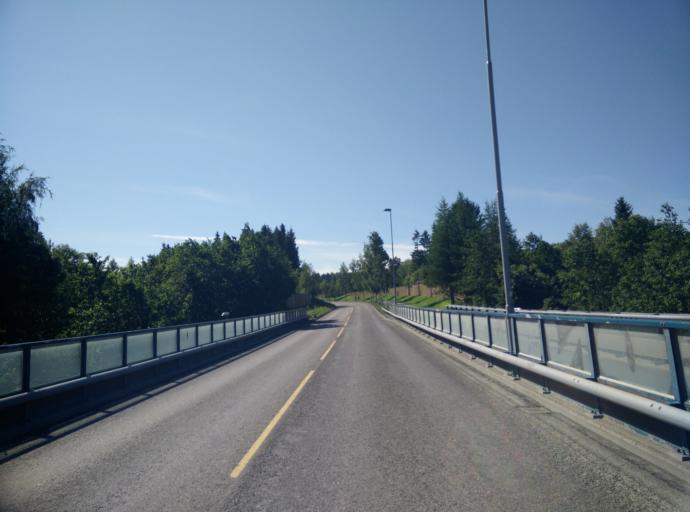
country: NO
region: Sor-Trondelag
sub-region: Trondheim
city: Trondheim
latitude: 63.3882
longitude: 10.3371
